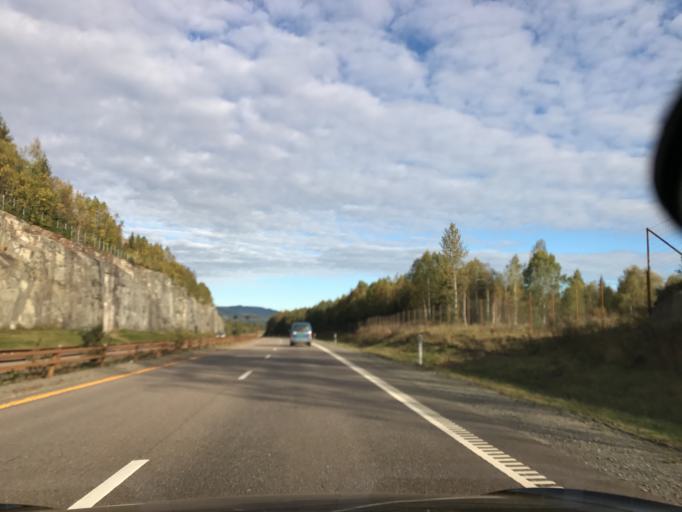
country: NO
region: Akershus
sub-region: Eidsvoll
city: Eidsvoll
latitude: 60.3516
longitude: 11.2087
